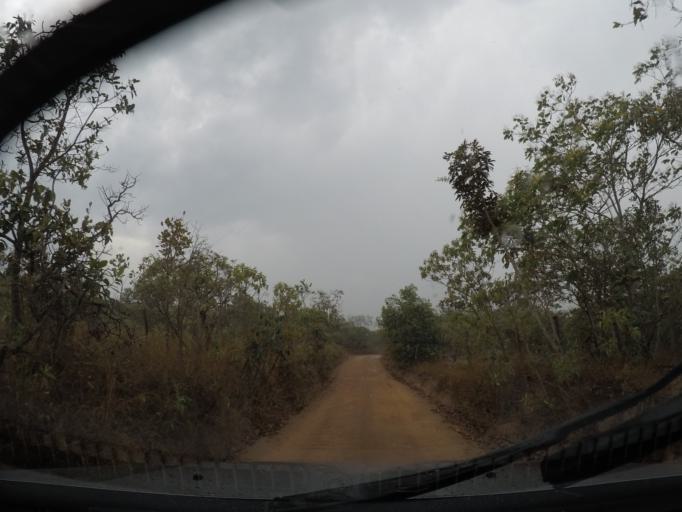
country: BR
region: Goias
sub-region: Pirenopolis
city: Pirenopolis
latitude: -15.8346
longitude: -48.8848
